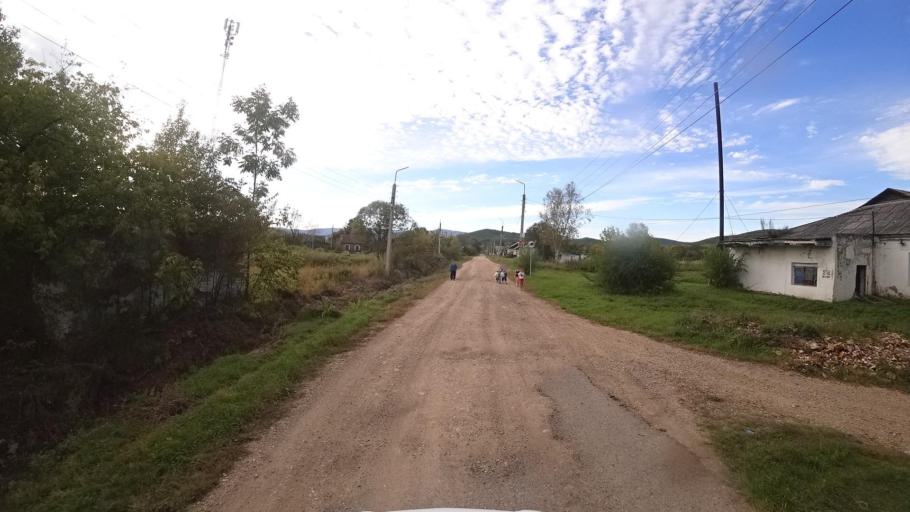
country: RU
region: Primorskiy
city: Dostoyevka
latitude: 44.3460
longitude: 133.4132
